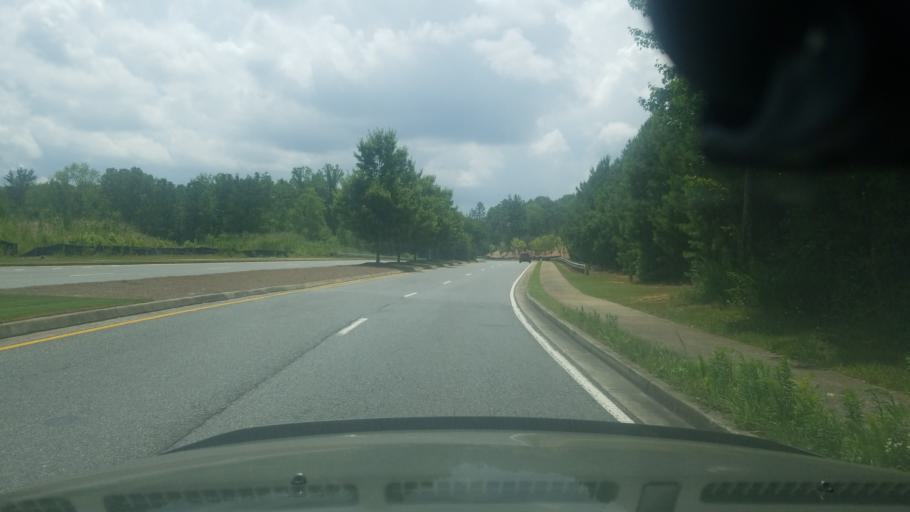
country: US
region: Georgia
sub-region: Fulton County
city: Johns Creek
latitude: 34.0981
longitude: -84.1705
